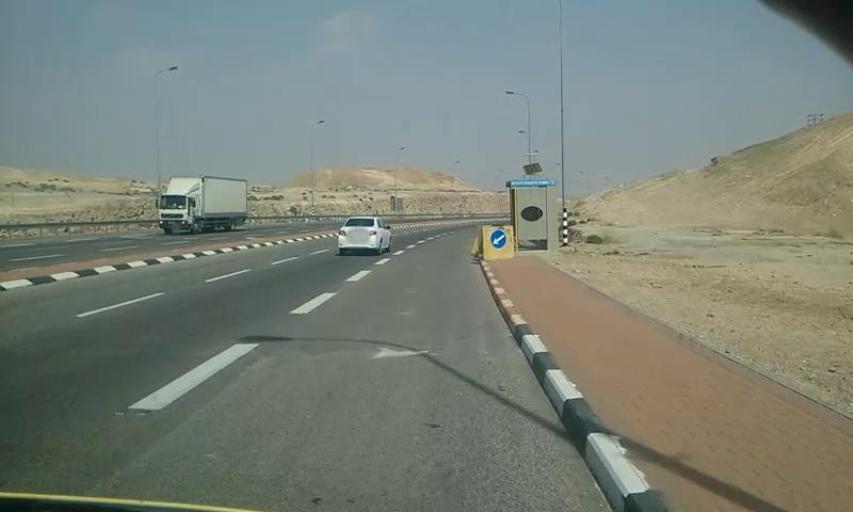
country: PS
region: West Bank
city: Jericho
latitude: 31.7985
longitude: 35.4285
